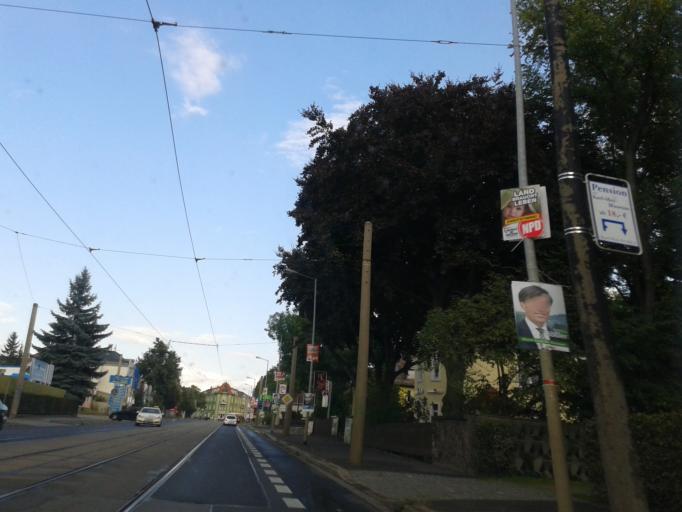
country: DE
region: Saxony
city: Radebeul
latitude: 51.1037
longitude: 13.6703
